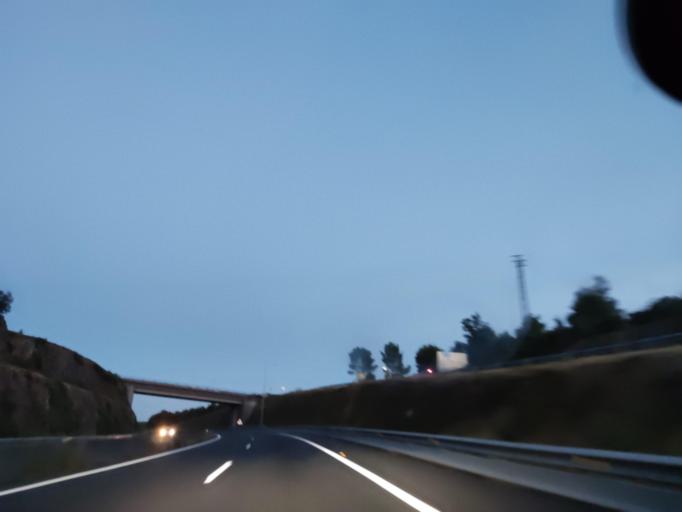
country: ES
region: Galicia
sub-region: Provincia da Coruna
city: Boiro
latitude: 42.6583
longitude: -8.8827
